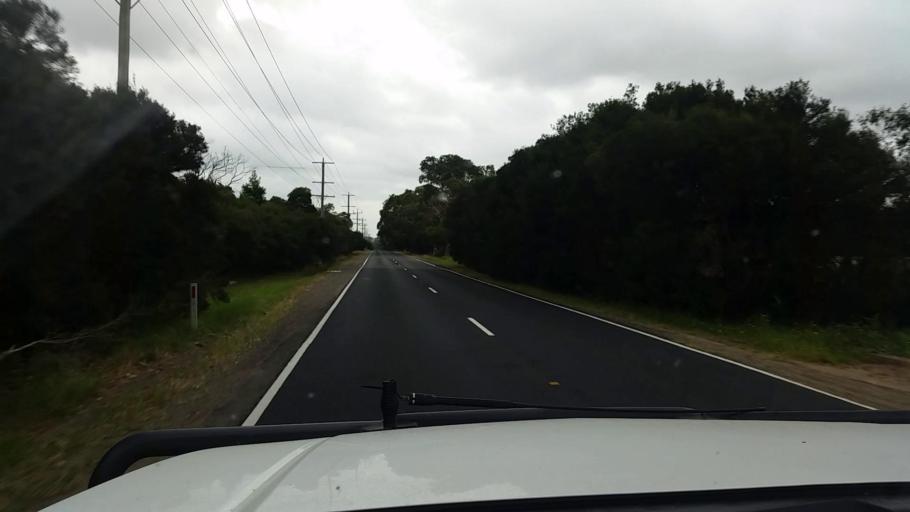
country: AU
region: Victoria
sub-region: Mornington Peninsula
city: Somerville
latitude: -38.2139
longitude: 145.1565
